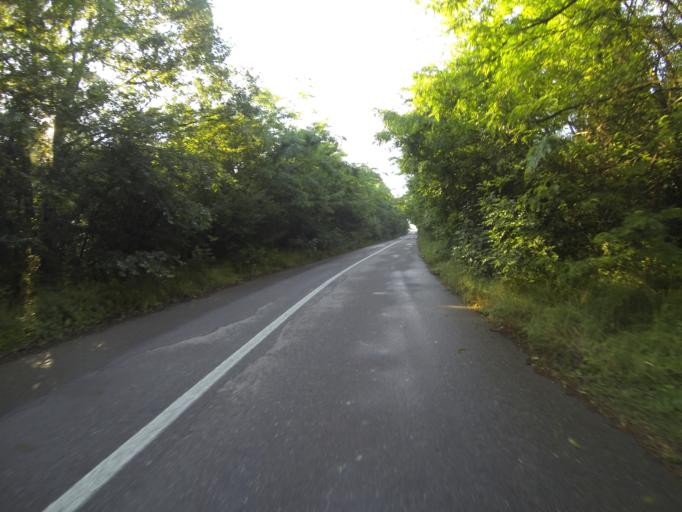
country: RO
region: Dolj
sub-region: Comuna Tuglui
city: Tuglui
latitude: 44.1749
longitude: 23.8169
